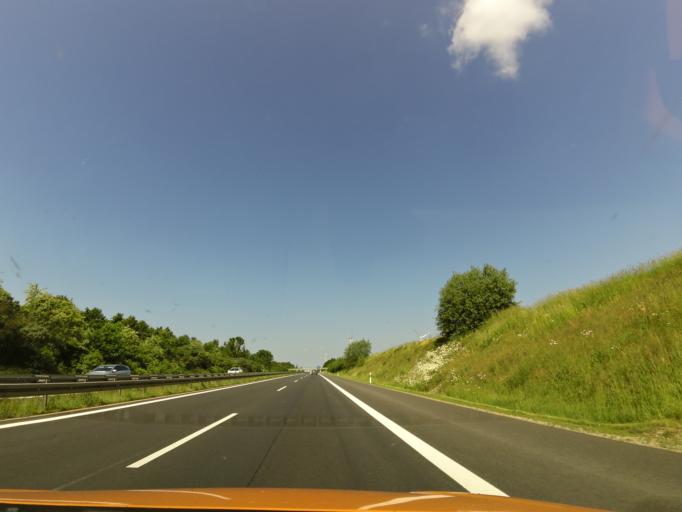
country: DE
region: Brandenburg
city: Gerdshagen
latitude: 53.2210
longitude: 12.2320
